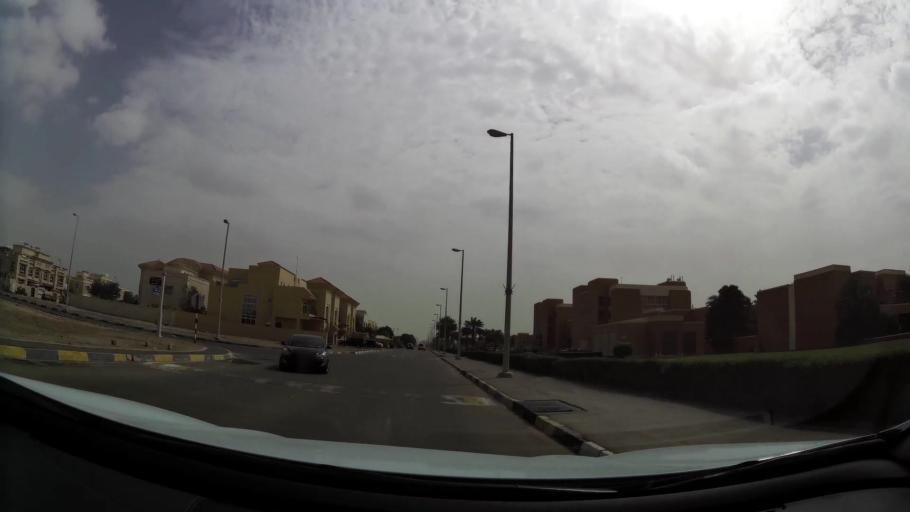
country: AE
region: Abu Dhabi
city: Abu Dhabi
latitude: 24.3942
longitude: 54.4923
